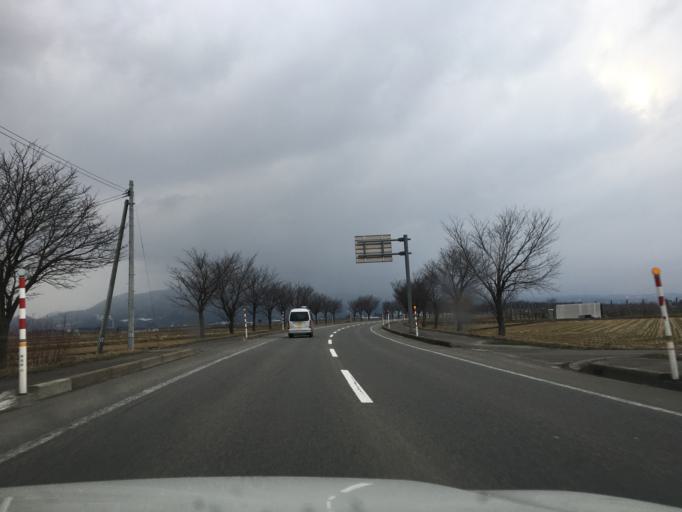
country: JP
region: Aomori
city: Kuroishi
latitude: 40.5701
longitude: 140.5665
